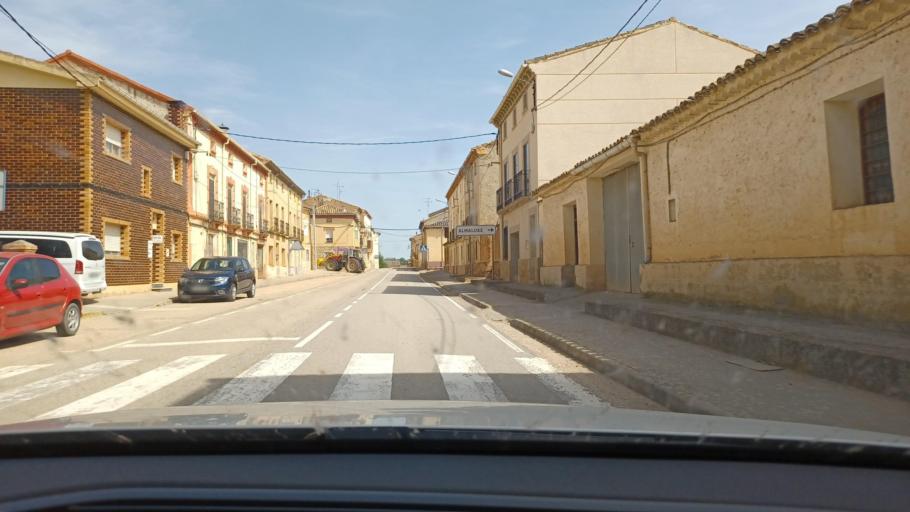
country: ES
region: Castille and Leon
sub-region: Provincia de Soria
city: Monteagudo de las Vicarias
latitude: 41.3656
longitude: -2.1700
